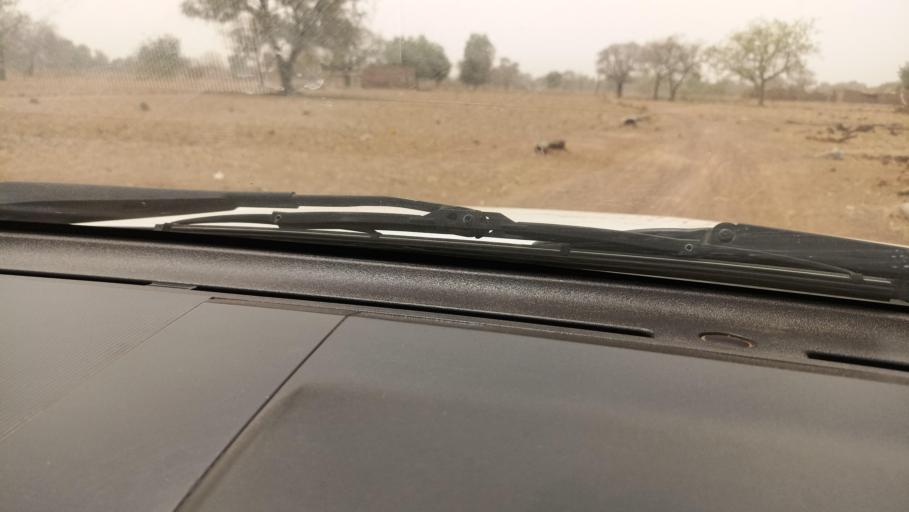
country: BF
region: Boucle du Mouhoun
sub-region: Province du Nayala
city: Toma
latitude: 12.8541
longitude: -2.7940
